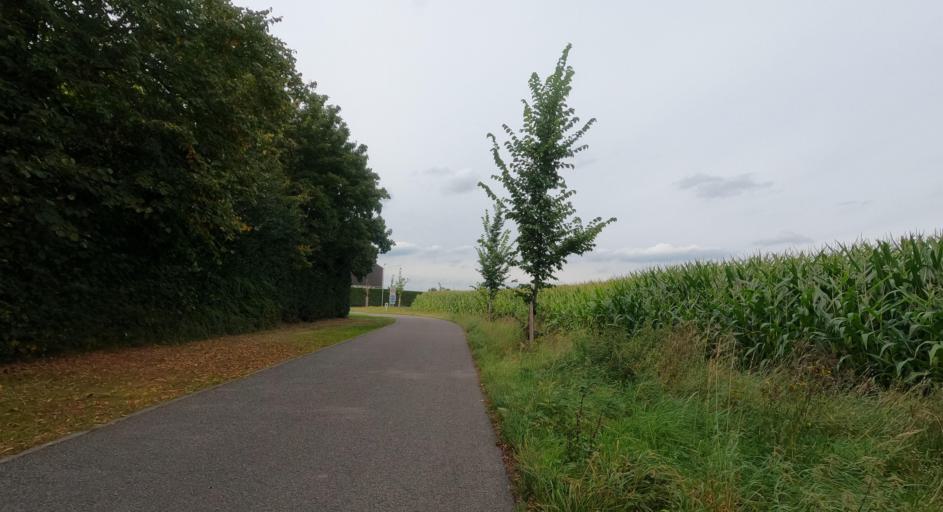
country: BE
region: Flanders
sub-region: Provincie Antwerpen
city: Essen
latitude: 51.4501
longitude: 4.5059
